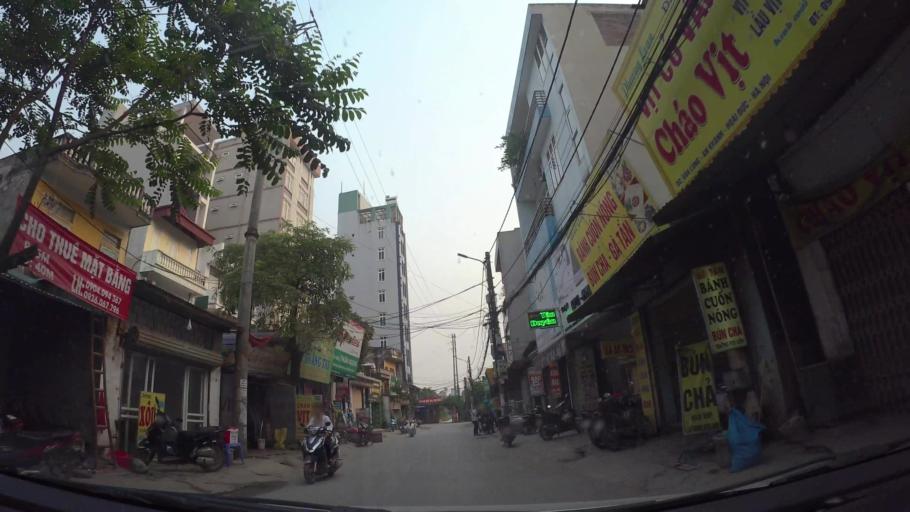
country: VN
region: Ha Noi
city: Cau Dien
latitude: 21.0058
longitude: 105.7201
